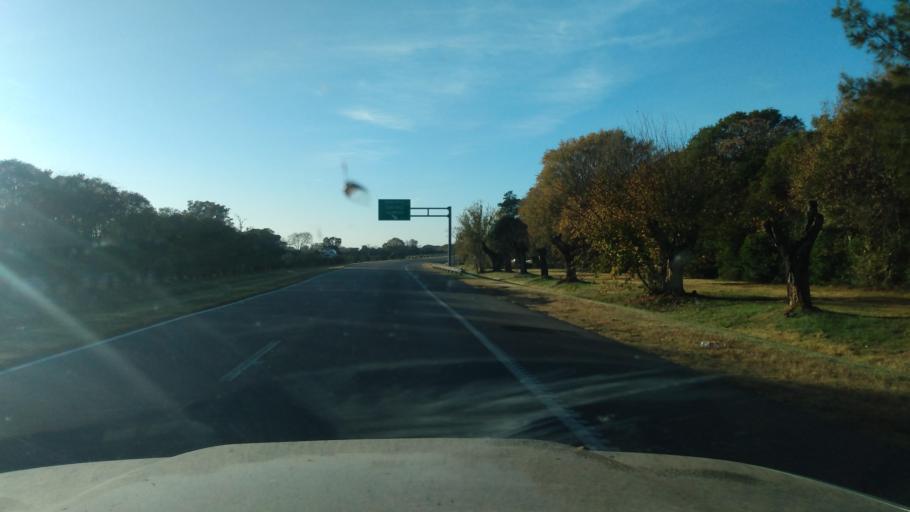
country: AR
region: Buenos Aires
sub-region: Partido de Lujan
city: Lujan
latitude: -34.5476
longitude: -59.2036
